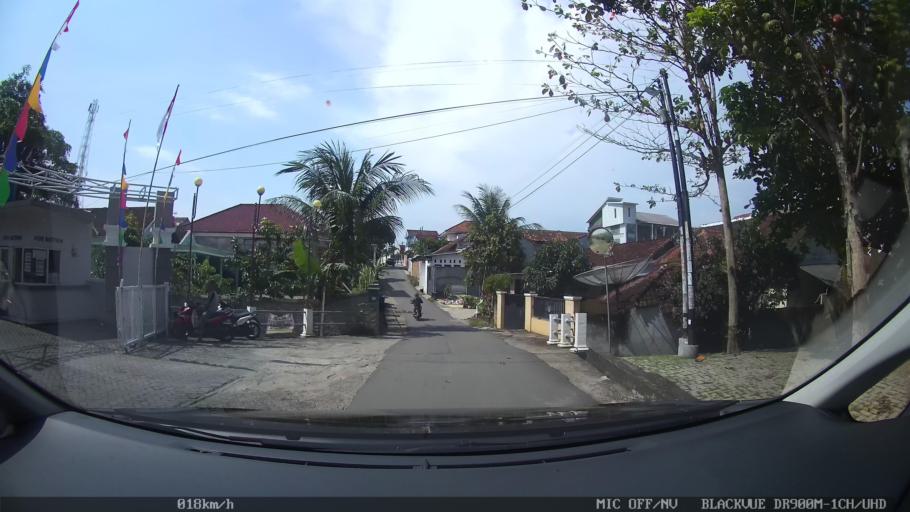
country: ID
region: Lampung
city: Kedaton
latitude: -5.3937
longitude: 105.2443
